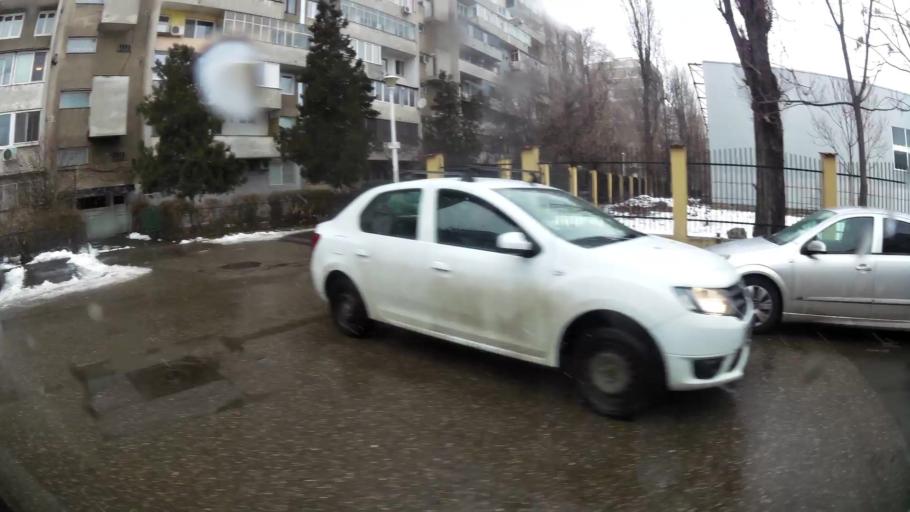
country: RO
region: Ilfov
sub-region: Comuna Chiajna
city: Rosu
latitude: 44.4261
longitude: 26.0505
